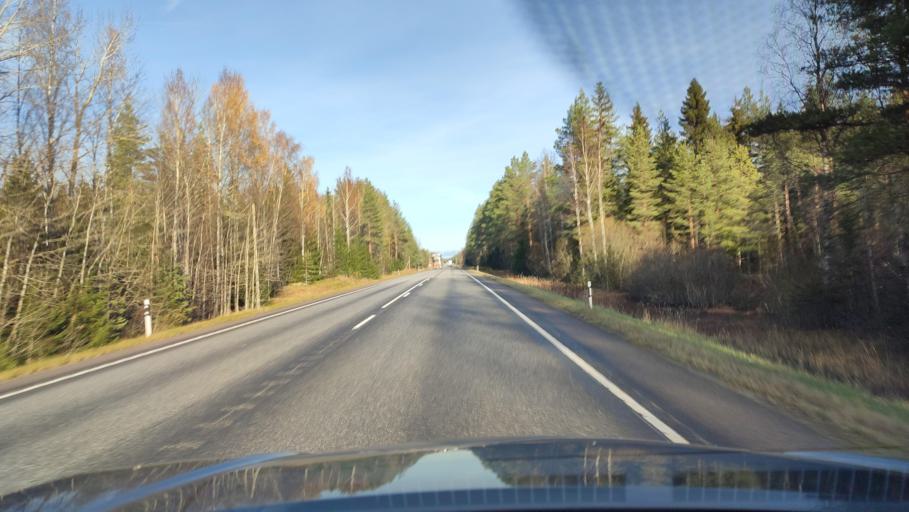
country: FI
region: Ostrobothnia
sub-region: Vaasa
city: Malax
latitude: 62.8175
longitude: 21.6861
